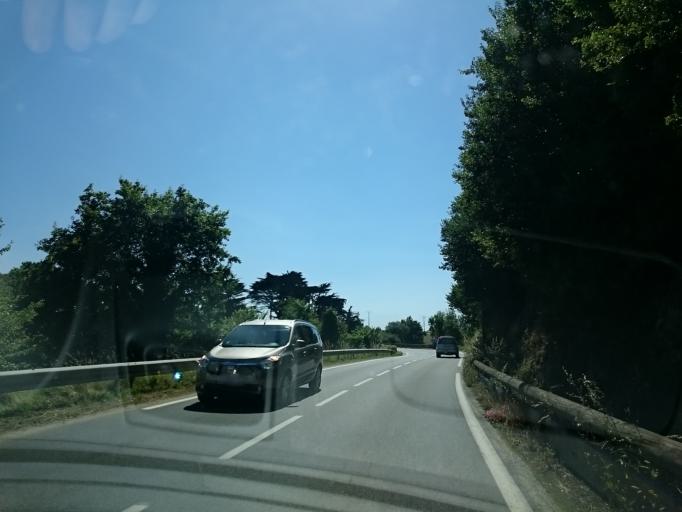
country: FR
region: Brittany
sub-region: Departement d'Ille-et-Vilaine
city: Saint-Coulomb
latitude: 48.6735
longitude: -1.9291
